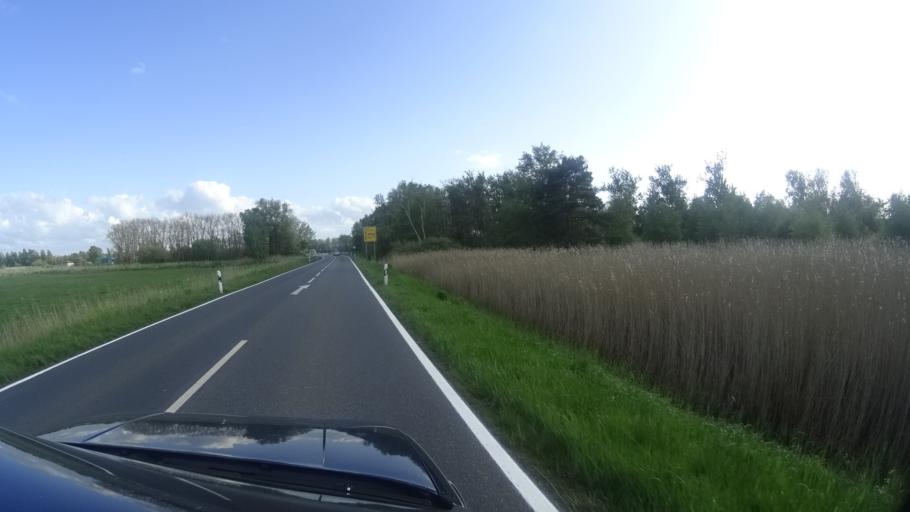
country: DE
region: Mecklenburg-Vorpommern
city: Ostseebad Dierhagen
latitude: 54.2986
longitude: 12.3517
